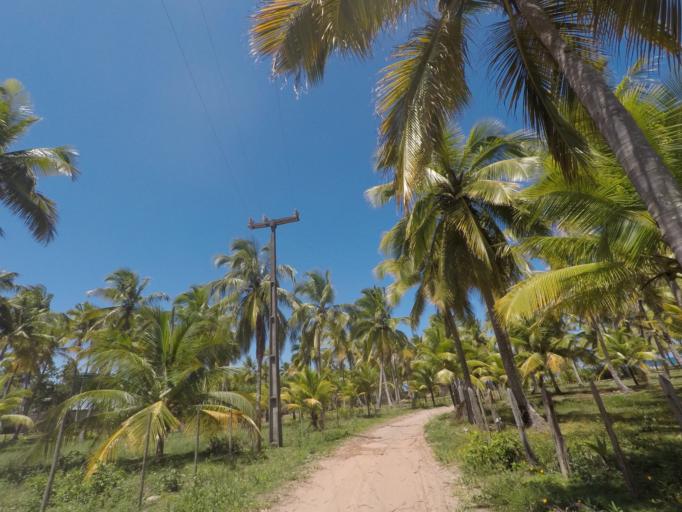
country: BR
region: Bahia
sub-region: Marau
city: Marau
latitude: -14.0056
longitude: -38.9452
